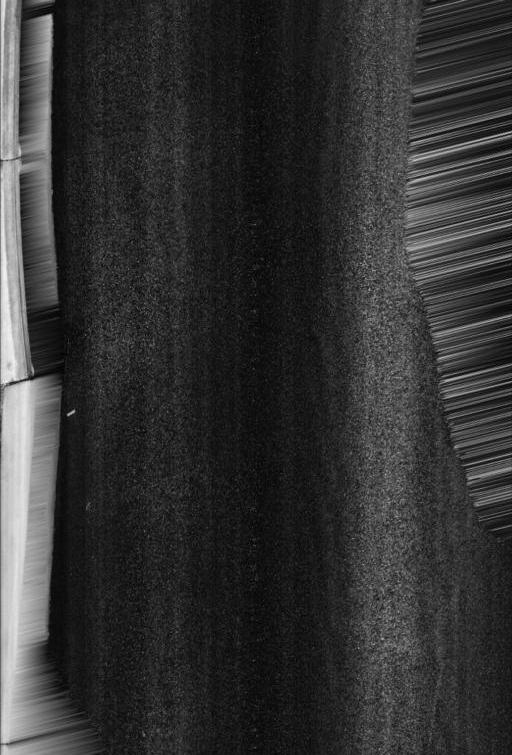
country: US
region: Virginia
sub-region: Arlington County
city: Arlington
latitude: 38.9158
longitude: -77.0841
